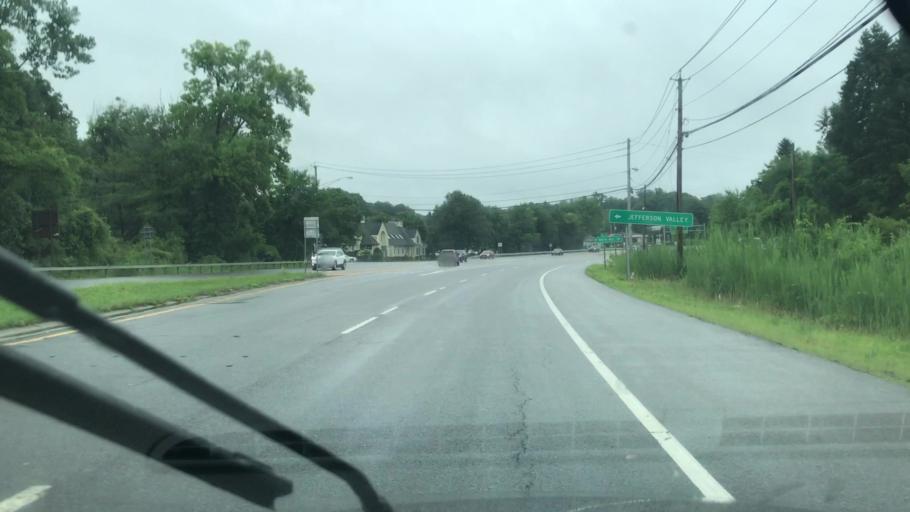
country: US
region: New York
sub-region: Westchester County
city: Shrub Oak
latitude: 41.3325
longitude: -73.8143
